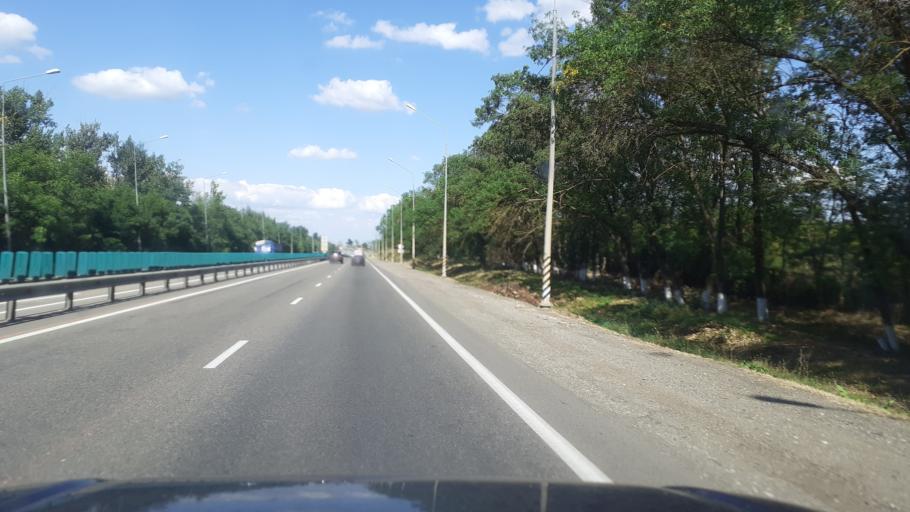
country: RU
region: Krasnodarskiy
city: Severskaya
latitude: 44.8347
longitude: 38.6835
